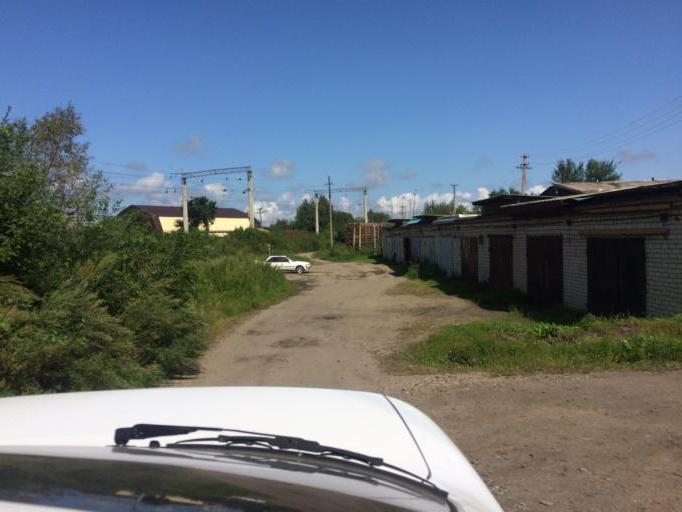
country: RU
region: Primorskiy
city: Dal'nerechensk
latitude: 45.9387
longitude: 133.7335
